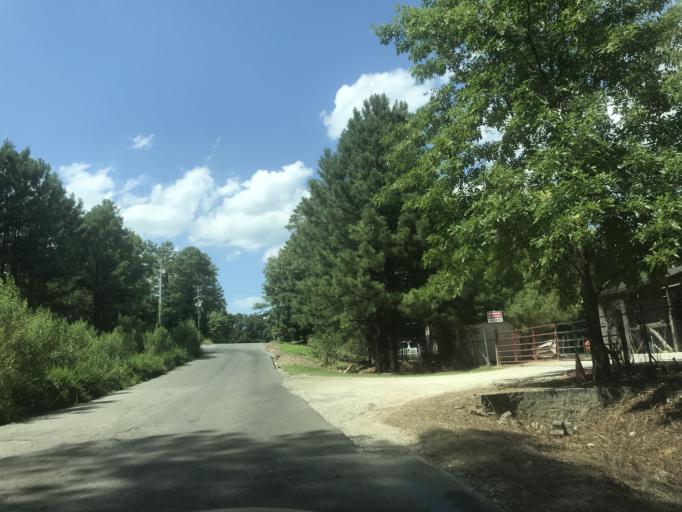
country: US
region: North Carolina
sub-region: Wake County
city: Morrisville
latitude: 35.8904
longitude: -78.7444
